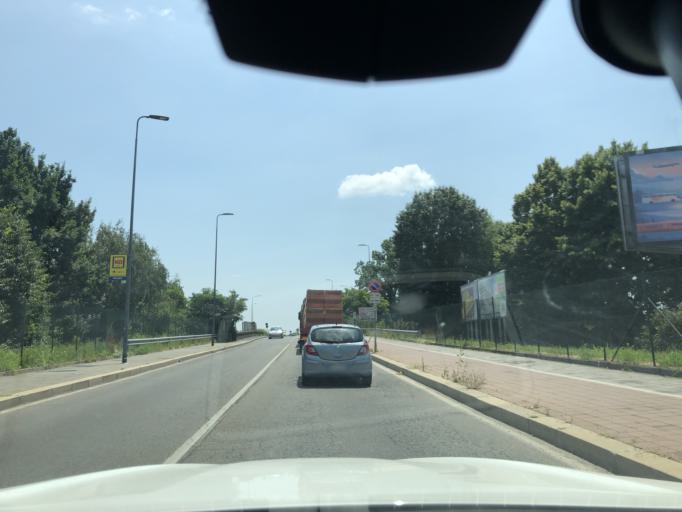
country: IT
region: Lombardy
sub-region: Citta metropolitana di Milano
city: Sesto San Giovanni
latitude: 45.5079
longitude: 9.2098
